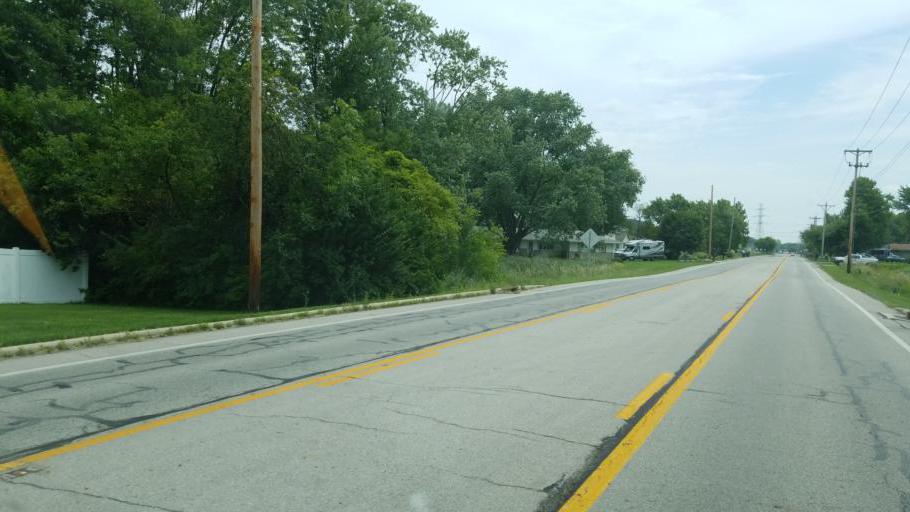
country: US
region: Ohio
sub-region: Franklin County
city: Hilliard
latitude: 40.0346
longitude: -83.1936
